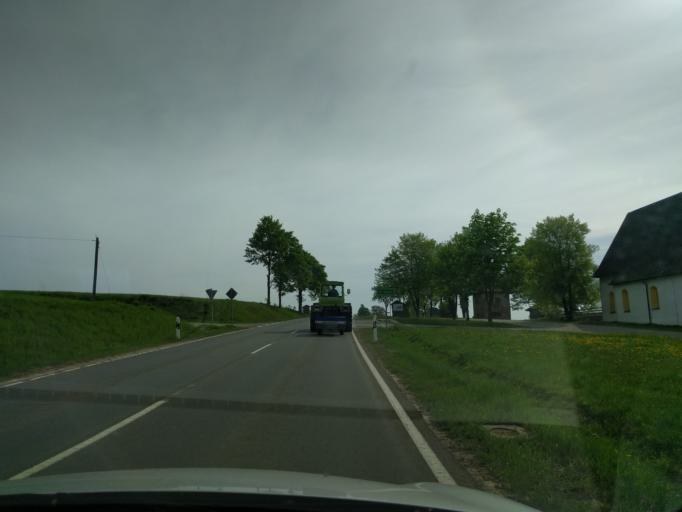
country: DE
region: Bavaria
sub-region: Upper Palatinate
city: Michelsneukirchen
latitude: 49.1202
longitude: 12.5352
